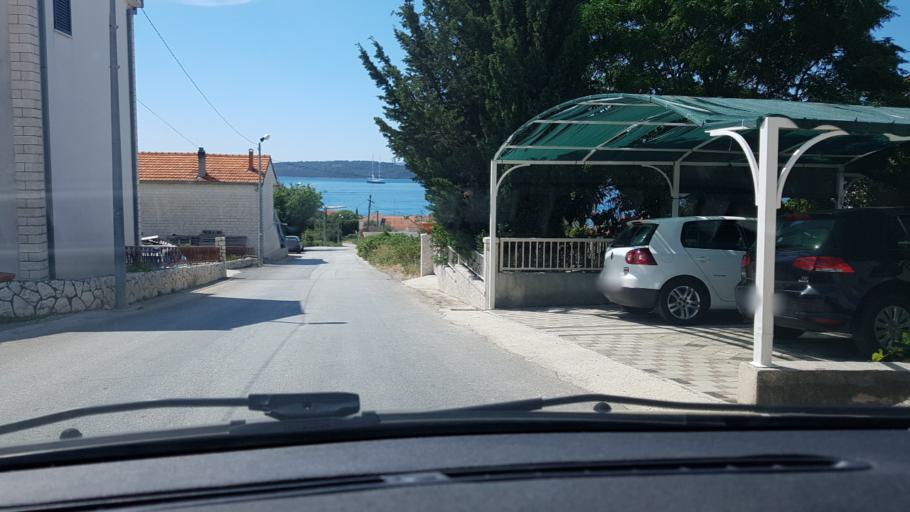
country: HR
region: Splitsko-Dalmatinska
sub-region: Grad Trogir
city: Trogir
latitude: 43.5216
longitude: 16.2275
